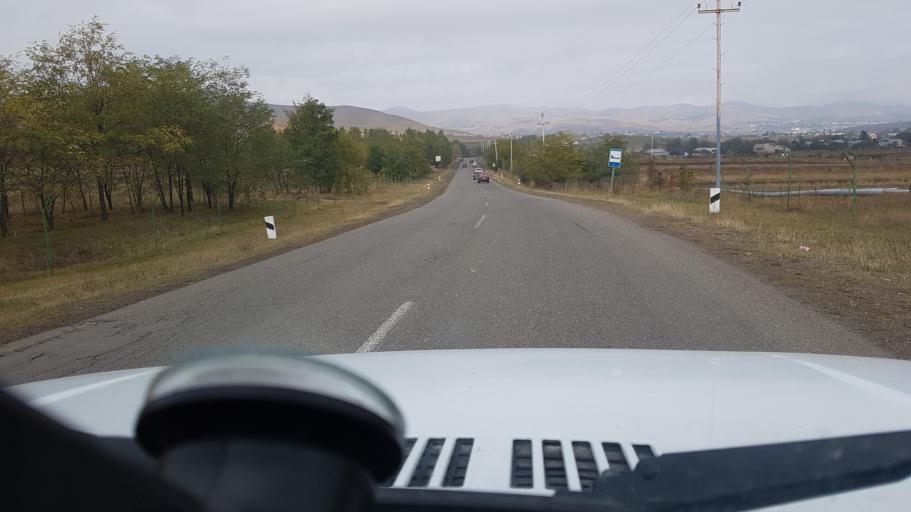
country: AZ
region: Gadabay Rayon
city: Ariqdam
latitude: 40.6269
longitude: 45.8158
